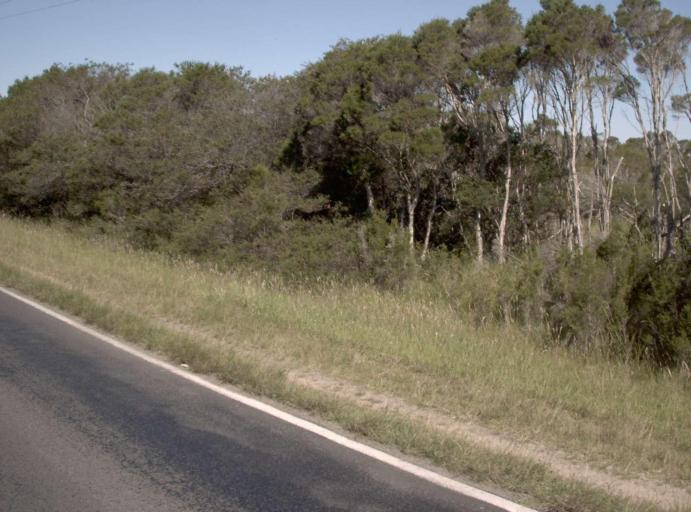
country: AU
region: Victoria
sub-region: Latrobe
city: Morwell
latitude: -38.6343
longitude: 146.5402
